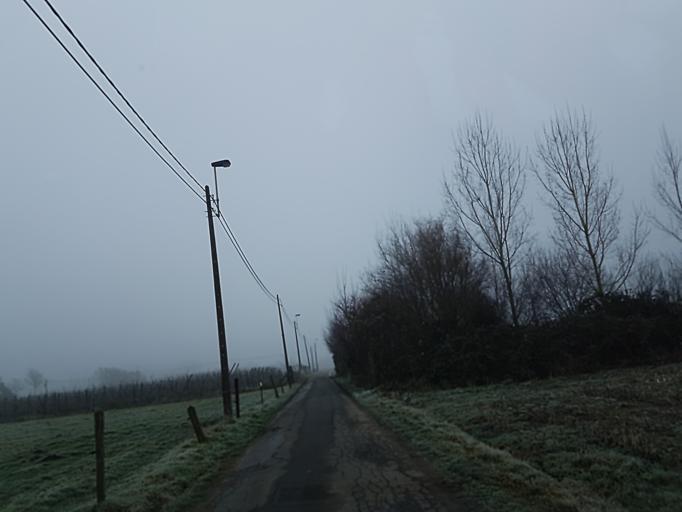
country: BE
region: Flanders
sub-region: Provincie Vlaams-Brabant
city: Kapelle-op-den-Bos
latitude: 50.9833
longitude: 4.4002
